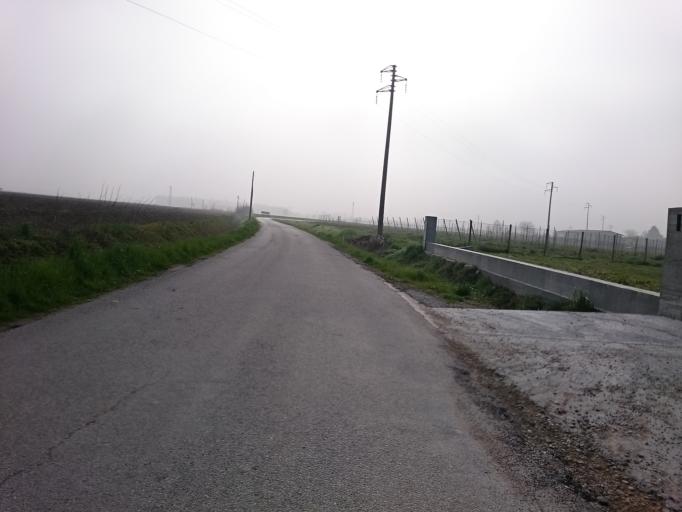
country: IT
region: Veneto
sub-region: Provincia di Padova
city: Due Carrare
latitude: 45.2917
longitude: 11.8366
